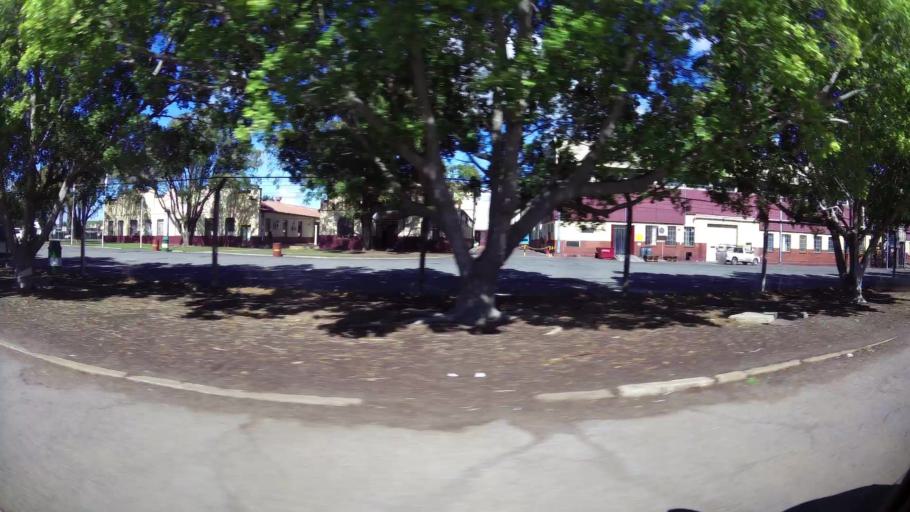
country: ZA
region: Western Cape
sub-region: Cape Winelands District Municipality
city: Ashton
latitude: -33.8330
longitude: 20.0647
